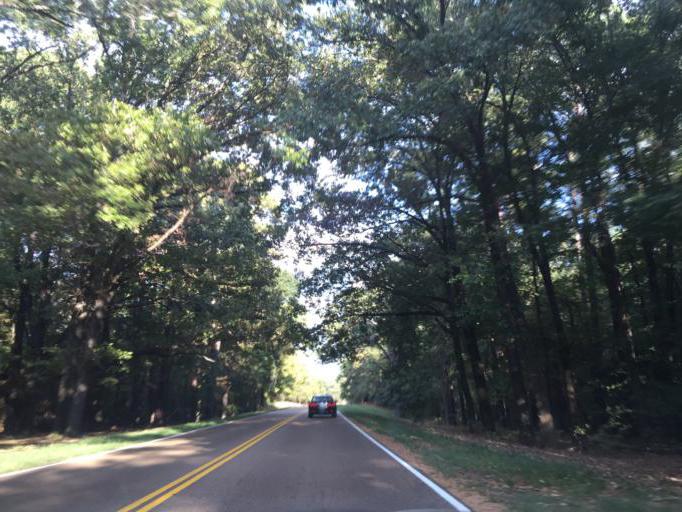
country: US
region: Mississippi
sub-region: Madison County
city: Ridgeland
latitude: 32.4272
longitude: -90.1187
